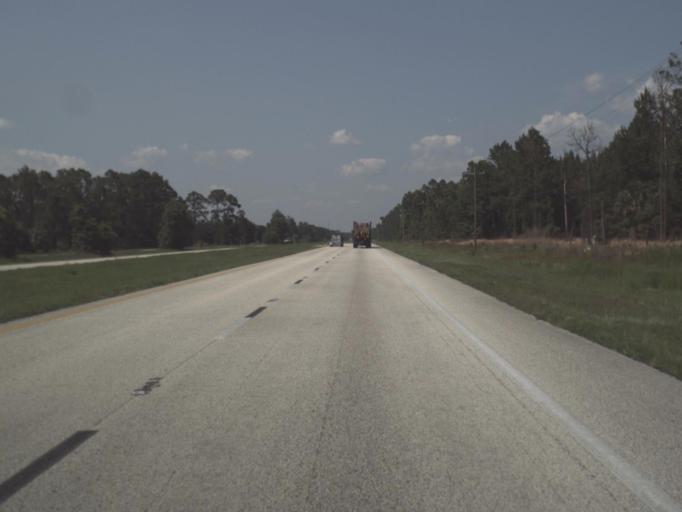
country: US
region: Florida
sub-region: Alachua County
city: Hawthorne
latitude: 29.5573
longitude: -82.0963
